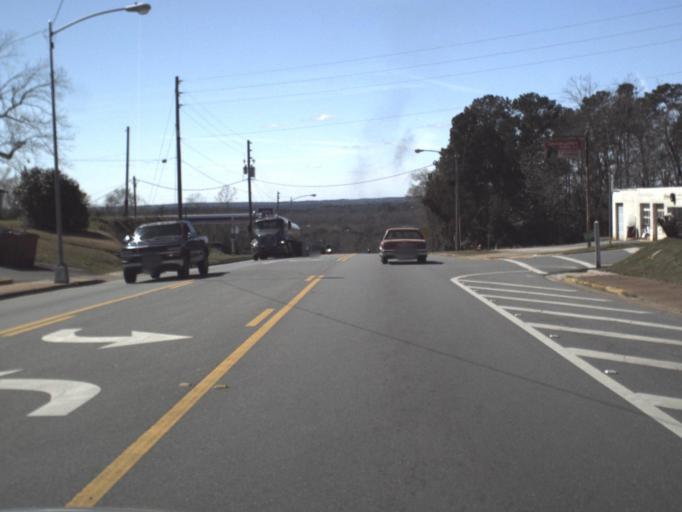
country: US
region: Florida
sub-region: Gadsden County
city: Chattahoochee
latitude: 30.7049
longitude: -84.8486
